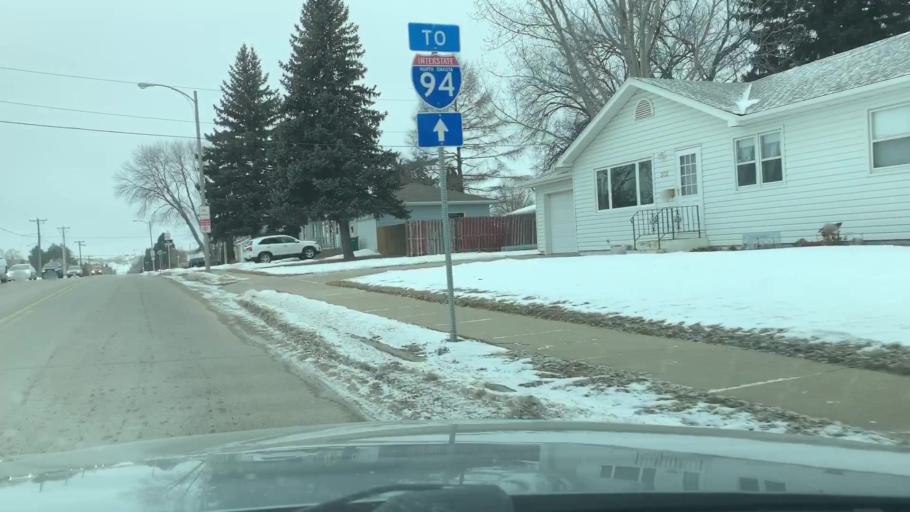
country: US
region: North Dakota
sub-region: Burleigh County
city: Bismarck
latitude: 46.8238
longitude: -100.7944
